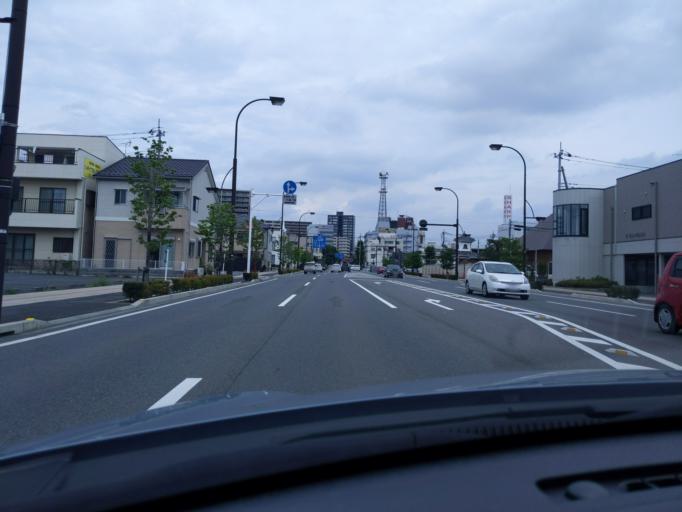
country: JP
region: Gunma
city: Maebashi-shi
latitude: 36.3864
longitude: 139.0677
